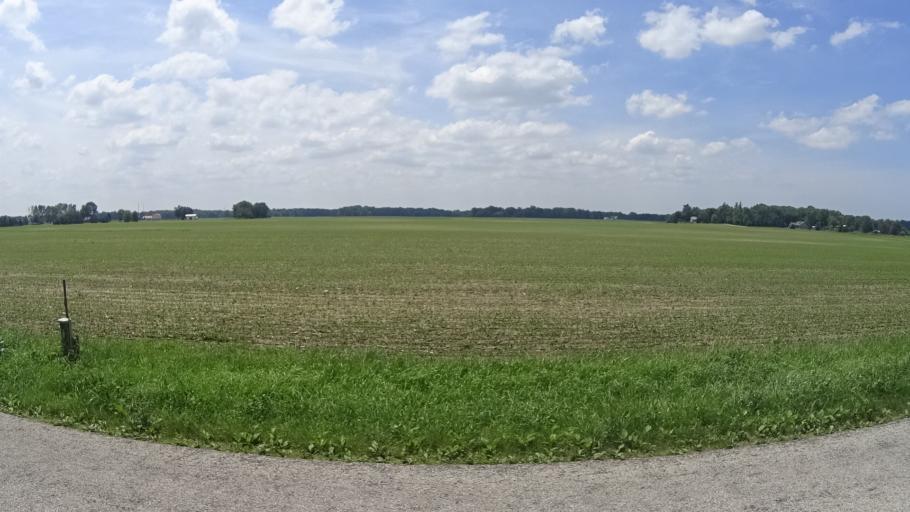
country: US
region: Ohio
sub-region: Erie County
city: Milan
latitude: 41.3190
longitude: -82.5356
